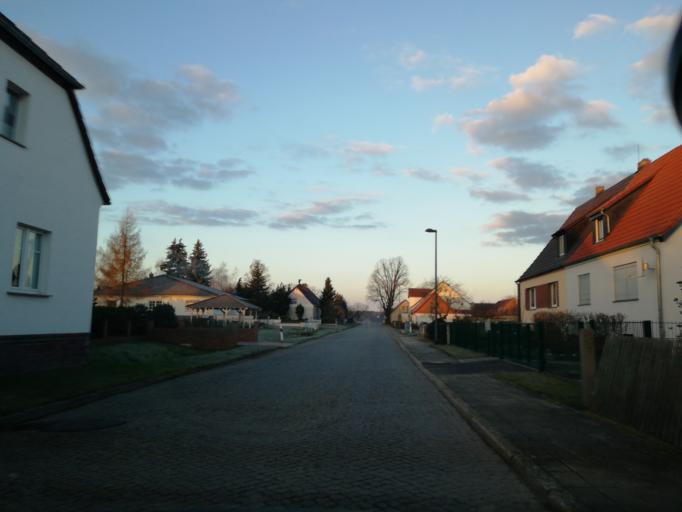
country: DE
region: Brandenburg
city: Calau
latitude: 51.7321
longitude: 13.9087
